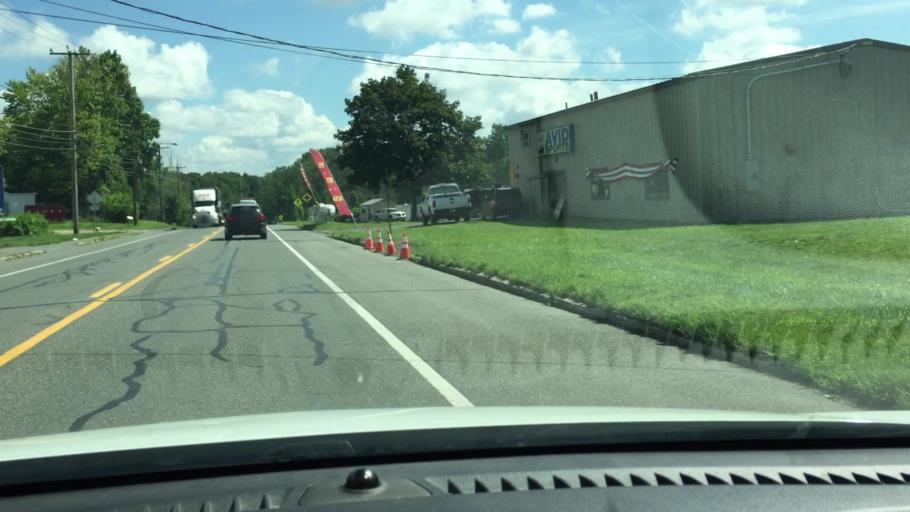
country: US
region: Massachusetts
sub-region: Berkshire County
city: Pittsfield
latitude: 42.4367
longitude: -73.3057
